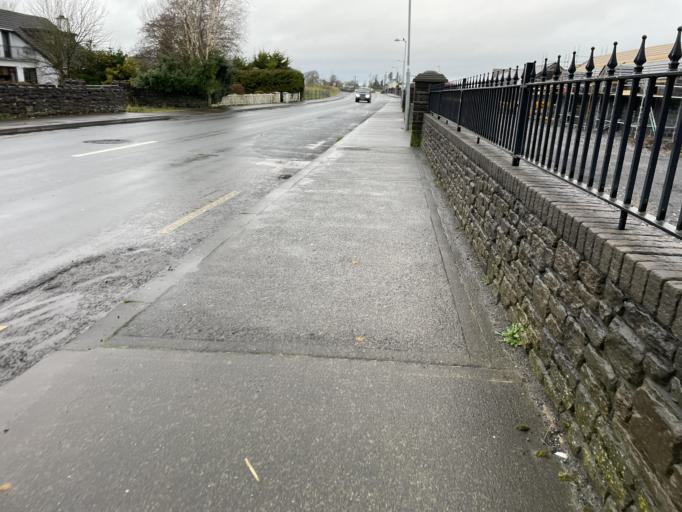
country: IE
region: Connaught
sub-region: County Galway
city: Tuam
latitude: 53.5137
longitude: -8.8635
